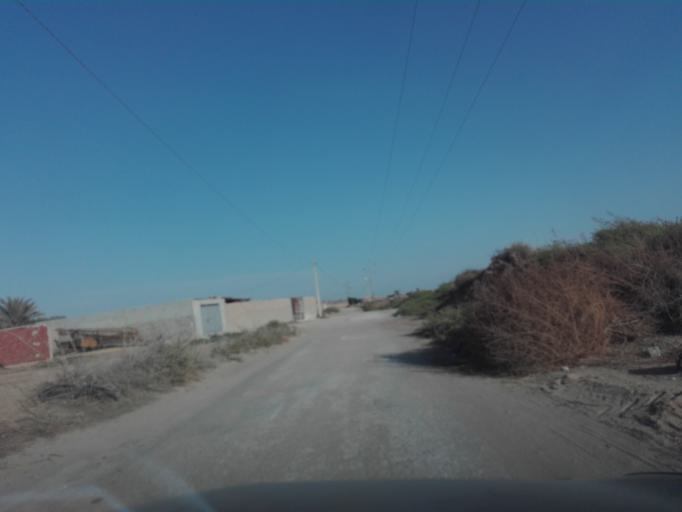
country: TN
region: Qabis
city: Gabes
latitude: 33.9588
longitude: 10.0622
